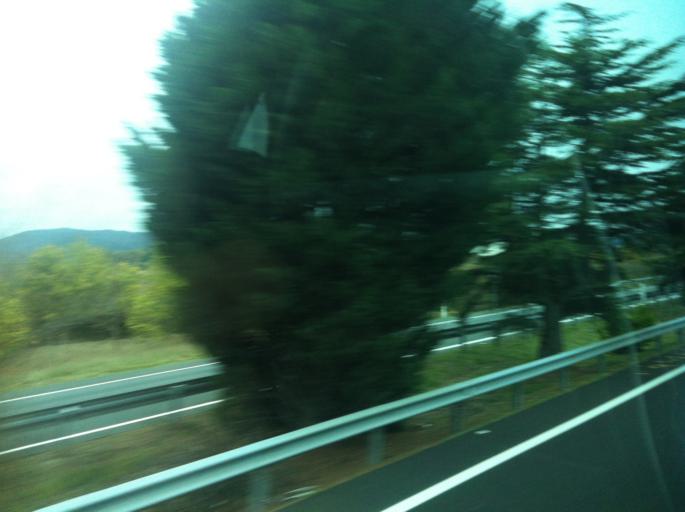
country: ES
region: Basque Country
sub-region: Provincia de Alava
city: Gasteiz / Vitoria
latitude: 42.8285
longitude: -2.7354
